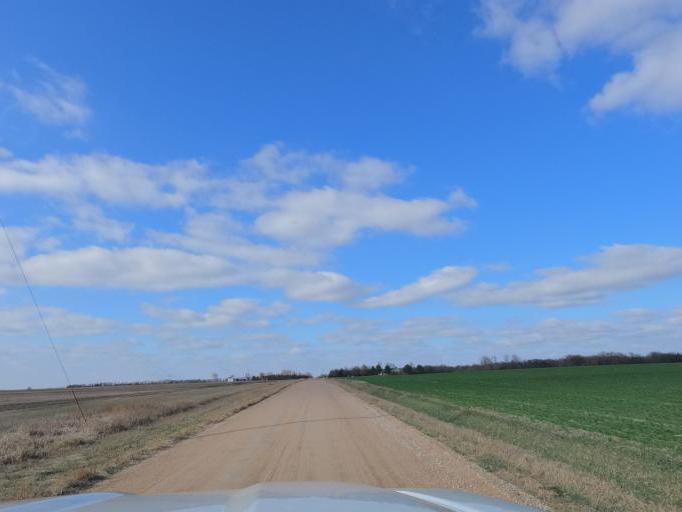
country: US
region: Kansas
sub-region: McPherson County
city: Inman
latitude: 38.2326
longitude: -97.8669
